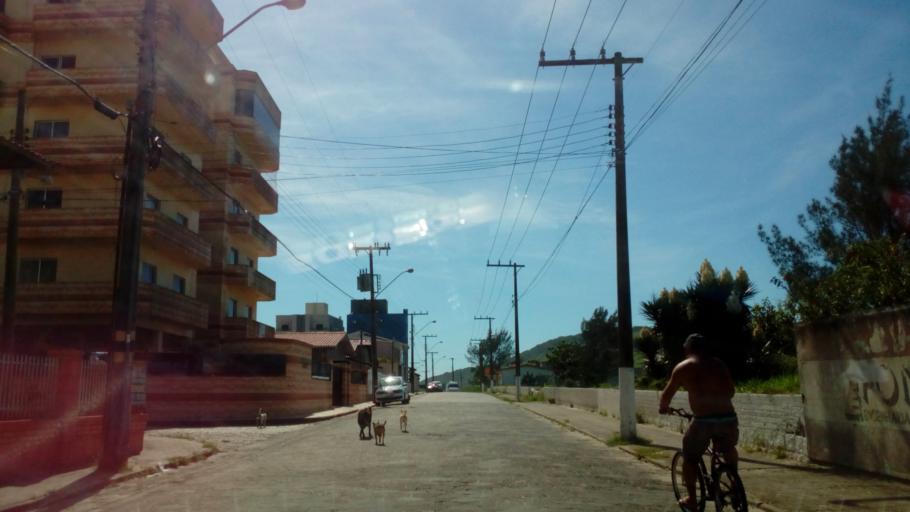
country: BR
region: Santa Catarina
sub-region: Laguna
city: Laguna
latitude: -28.4952
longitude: -48.7651
